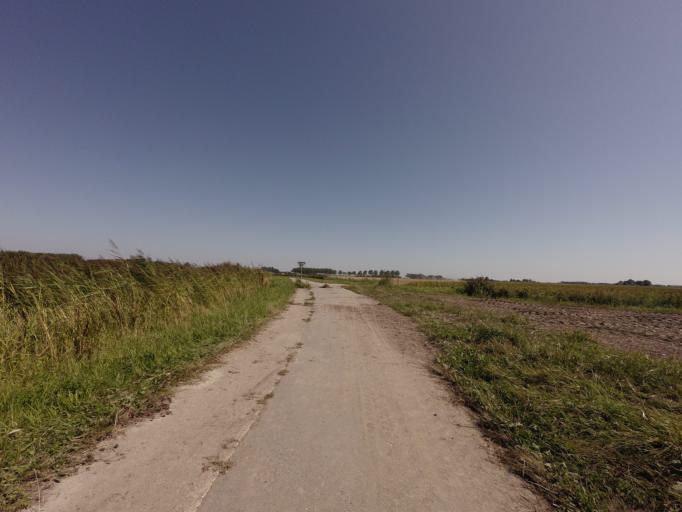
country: NL
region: Friesland
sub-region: Gemeente Dongeradeel
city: Anjum
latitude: 53.3969
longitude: 6.0760
